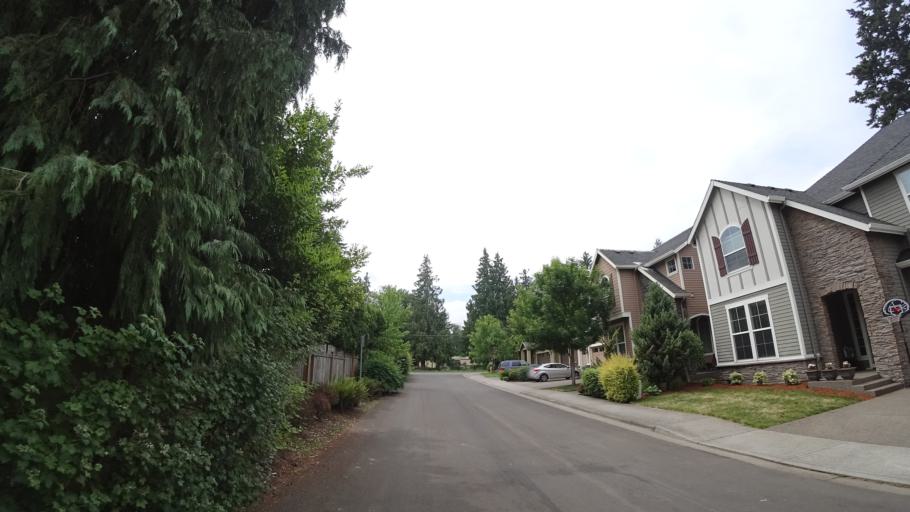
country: US
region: Oregon
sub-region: Washington County
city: Garden Home-Whitford
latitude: 45.4554
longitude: -122.7607
